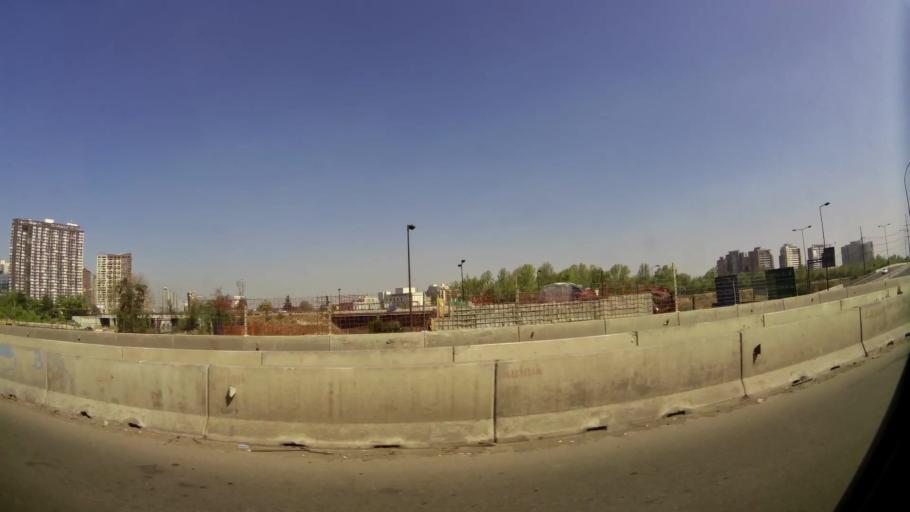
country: CL
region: Santiago Metropolitan
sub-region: Provincia de Santiago
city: Santiago
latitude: -33.4289
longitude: -70.6614
